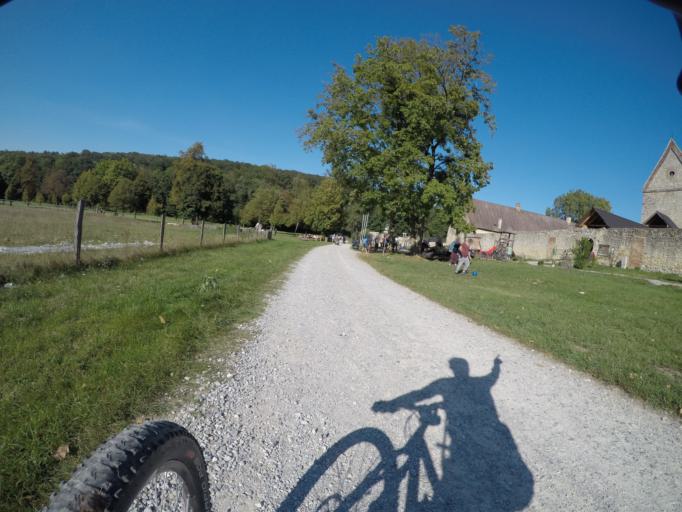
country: AT
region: Lower Austria
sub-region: Politischer Bezirk Bruck an der Leitha
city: Mannersdorf am Leithagebirge
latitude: 47.9534
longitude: 16.5993
